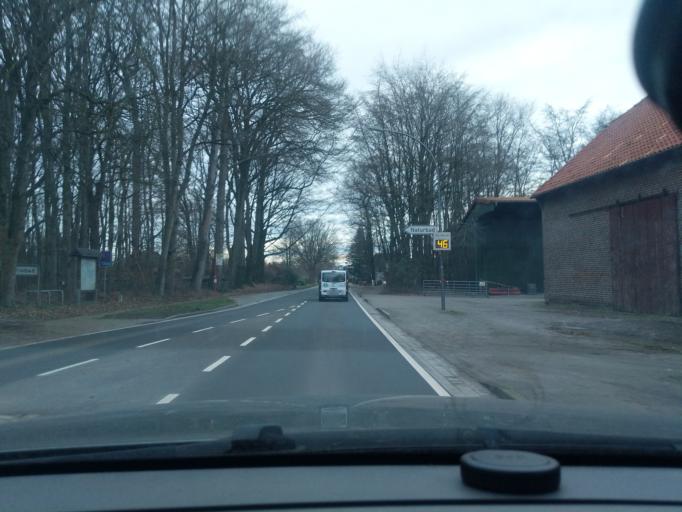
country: DE
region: Lower Saxony
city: Sauensiek
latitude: 53.3800
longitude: 9.5963
